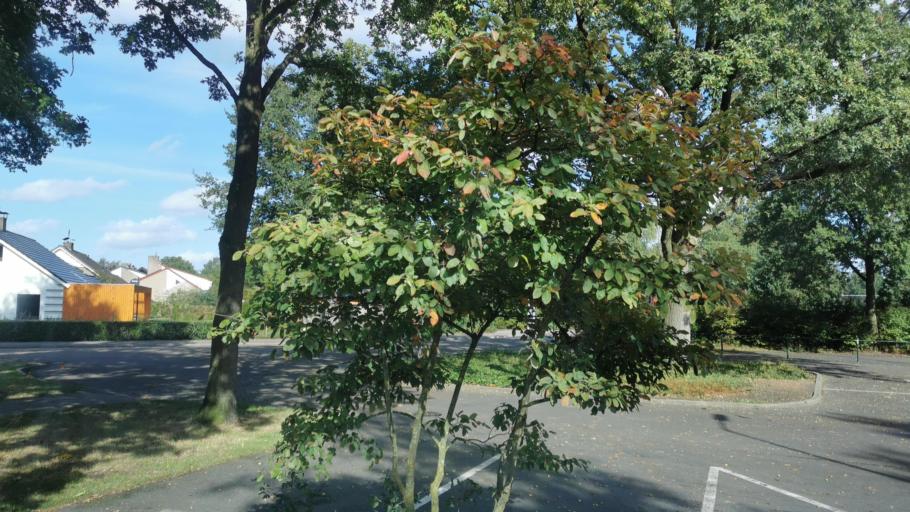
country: NL
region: Overijssel
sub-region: Gemeente Losser
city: Losser
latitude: 52.2686
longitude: 7.0138
